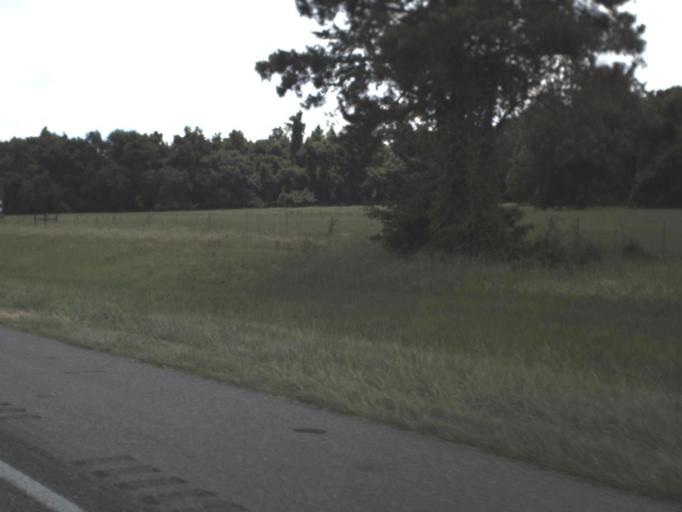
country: US
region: Florida
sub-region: Columbia County
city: Lake City
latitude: 30.0806
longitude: -82.6346
